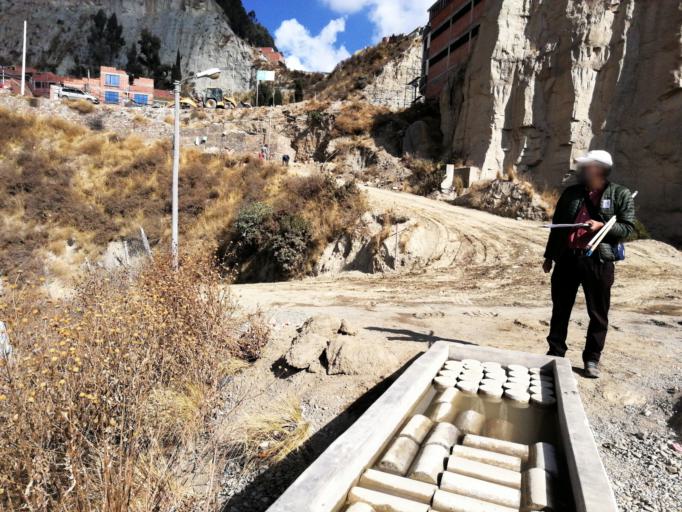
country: BO
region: La Paz
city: La Paz
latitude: -16.5259
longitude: -68.1370
